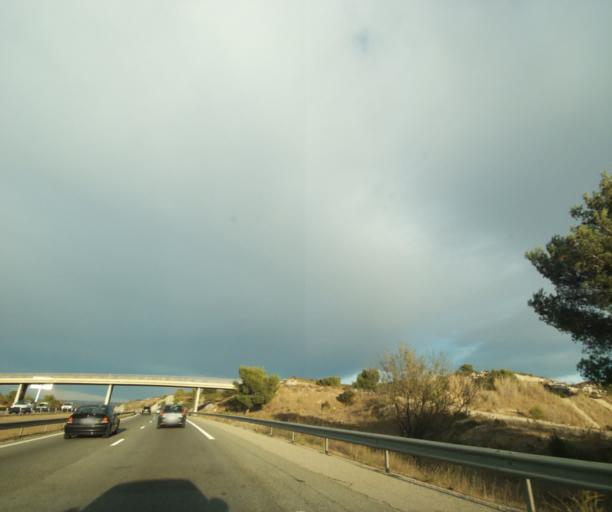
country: FR
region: Provence-Alpes-Cote d'Azur
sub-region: Departement des Bouches-du-Rhone
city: Ensues-la-Redonne
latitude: 43.3748
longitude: 5.1985
